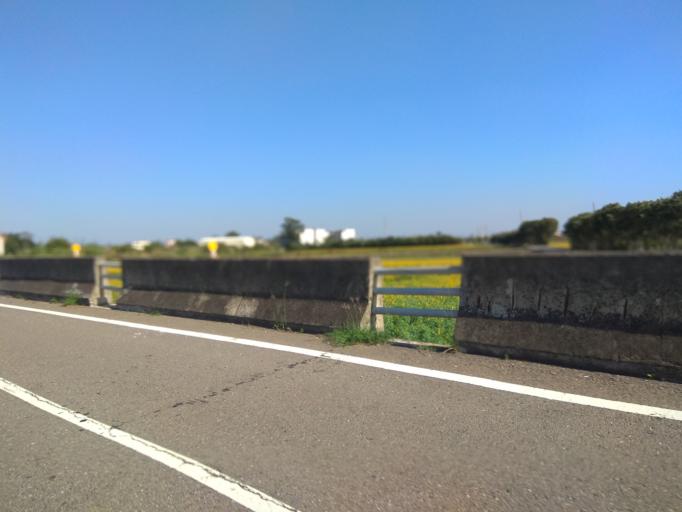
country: TW
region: Taiwan
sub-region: Hsinchu
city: Zhubei
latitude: 24.9908
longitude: 121.0330
